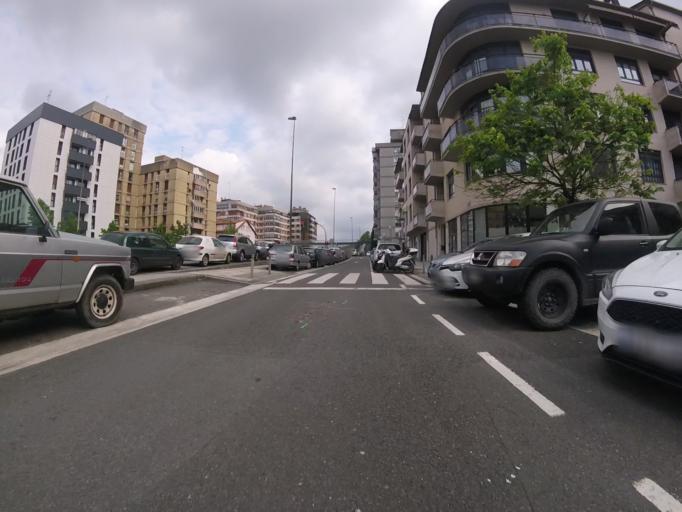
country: ES
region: Basque Country
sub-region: Provincia de Guipuzcoa
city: San Sebastian
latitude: 43.3094
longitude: -1.9675
